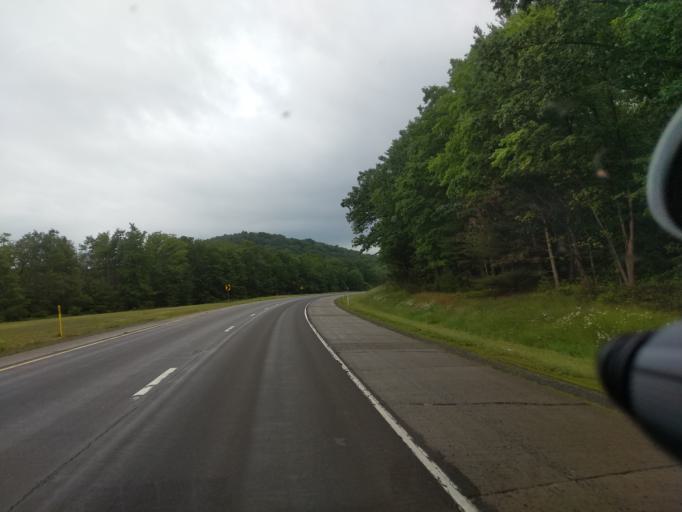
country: US
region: Pennsylvania
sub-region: Union County
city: Mifflinburg
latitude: 41.0412
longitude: -77.1360
